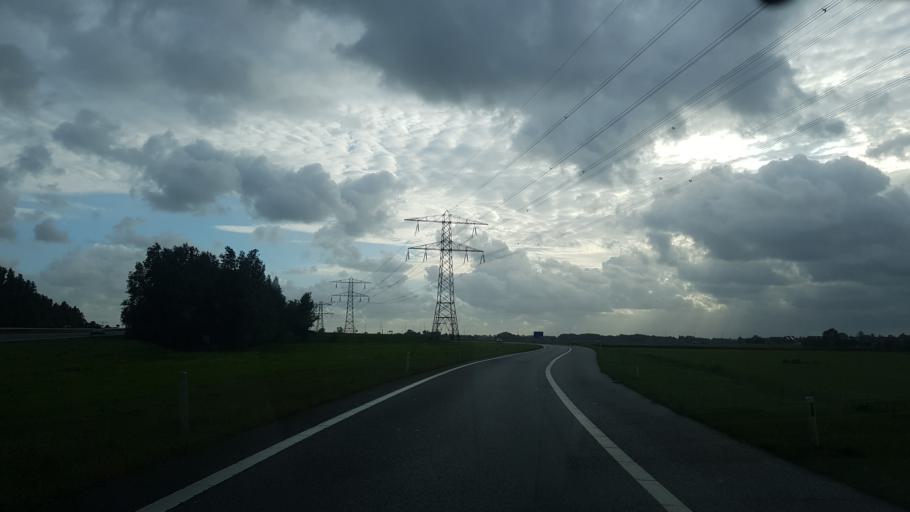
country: NL
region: Friesland
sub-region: Gemeente Boarnsterhim
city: Wergea
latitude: 53.1689
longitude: 5.8369
